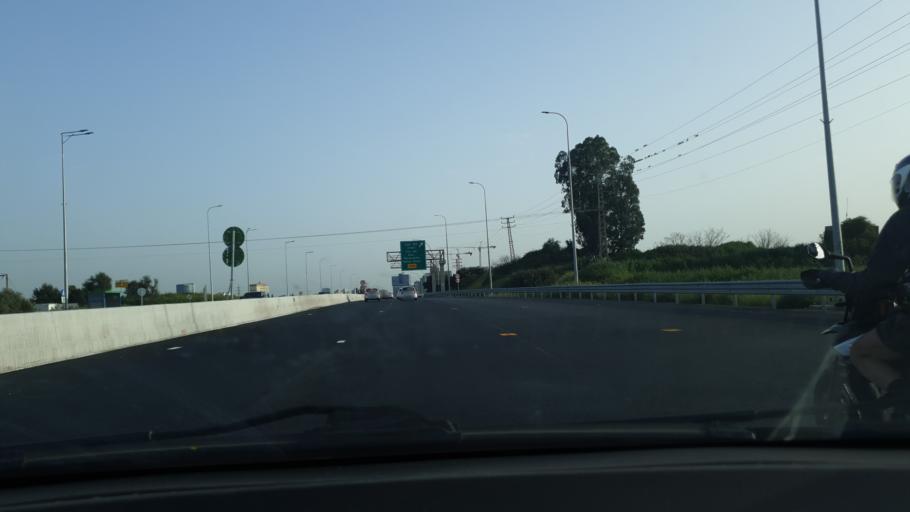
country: IL
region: Central District
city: Ra'anana
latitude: 32.2091
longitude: 34.8838
